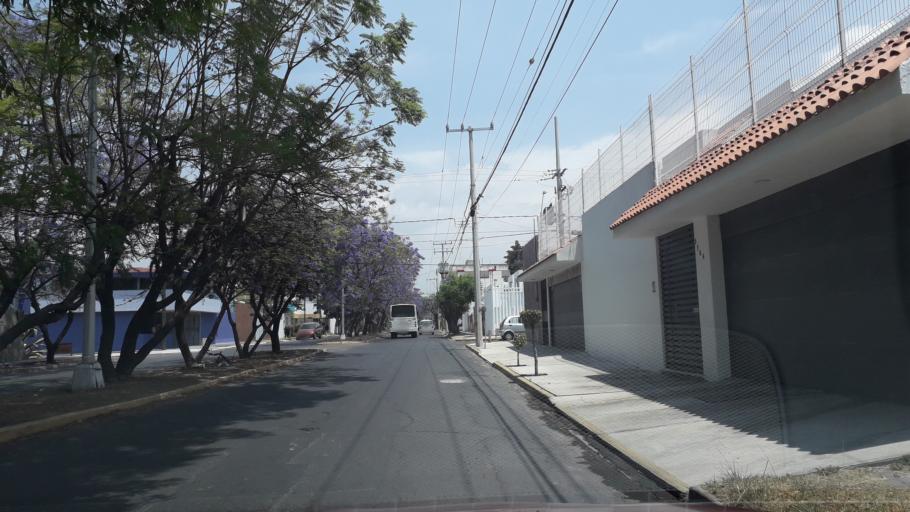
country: MX
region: Puebla
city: Puebla
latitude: 19.0229
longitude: -98.1940
